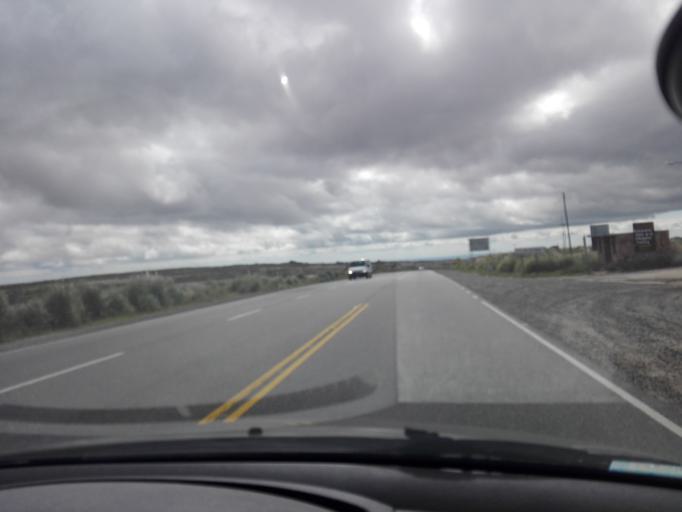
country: AR
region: Cordoba
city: Mina Clavero
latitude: -31.6173
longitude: -64.8746
